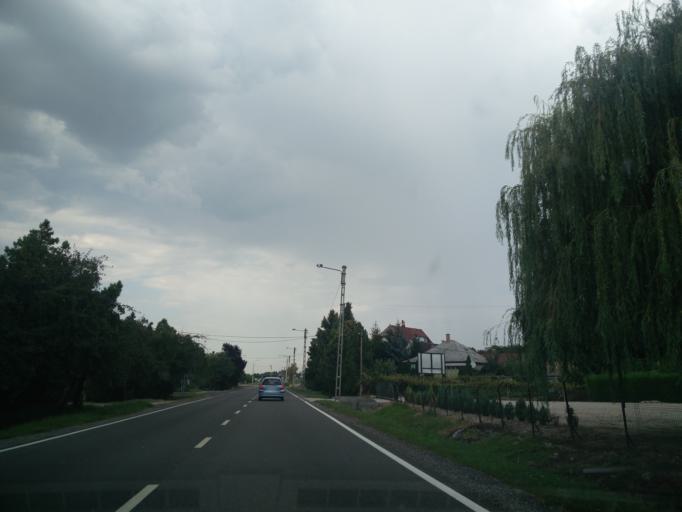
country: HU
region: Fejer
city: Polgardi
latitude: 47.0511
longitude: 18.3034
